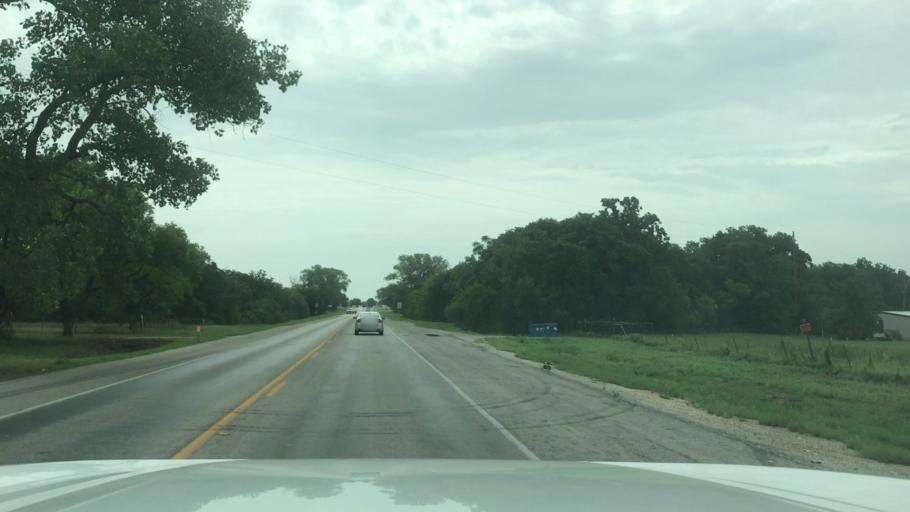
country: US
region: Texas
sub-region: Eastland County
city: Gorman
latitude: 32.2198
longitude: -98.6781
